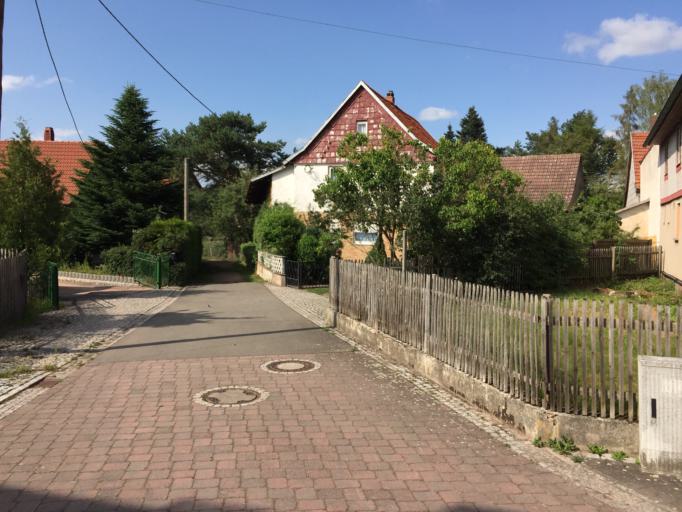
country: DE
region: Thuringia
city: Immelborn
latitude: 50.7849
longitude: 10.2704
